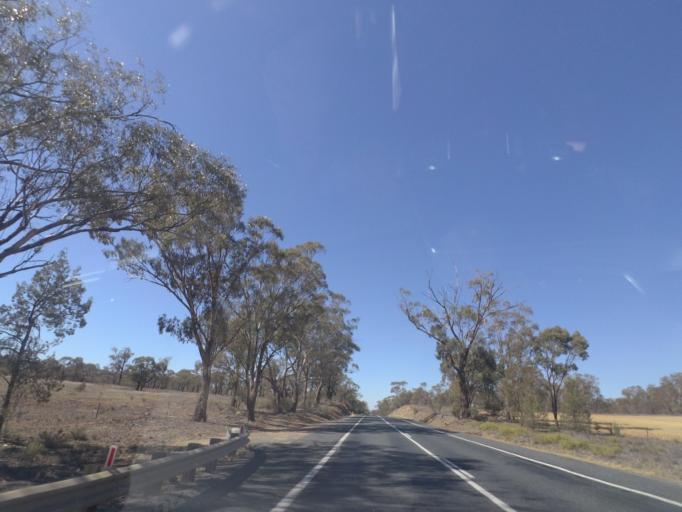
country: AU
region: New South Wales
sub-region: Bland
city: West Wyalong
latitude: -34.1658
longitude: 147.1159
